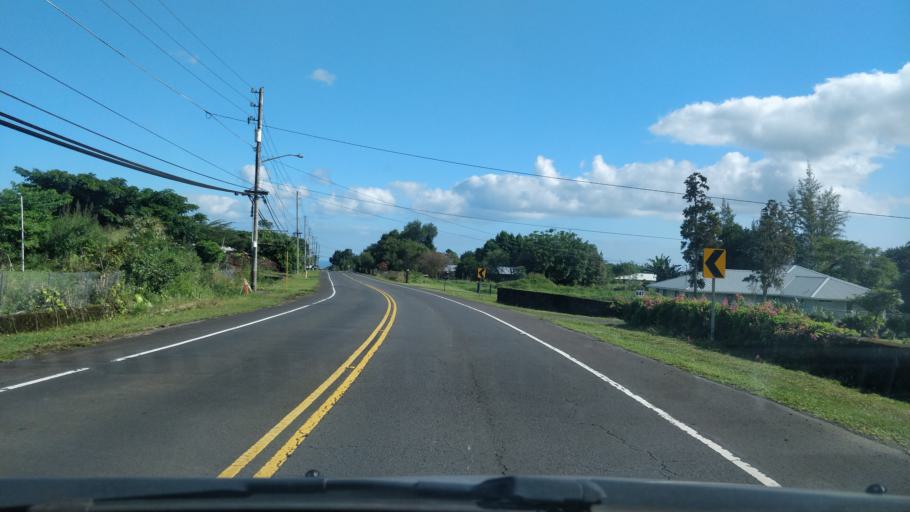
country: US
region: Hawaii
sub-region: Hawaii County
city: Hilo
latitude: 19.6668
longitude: -155.0965
